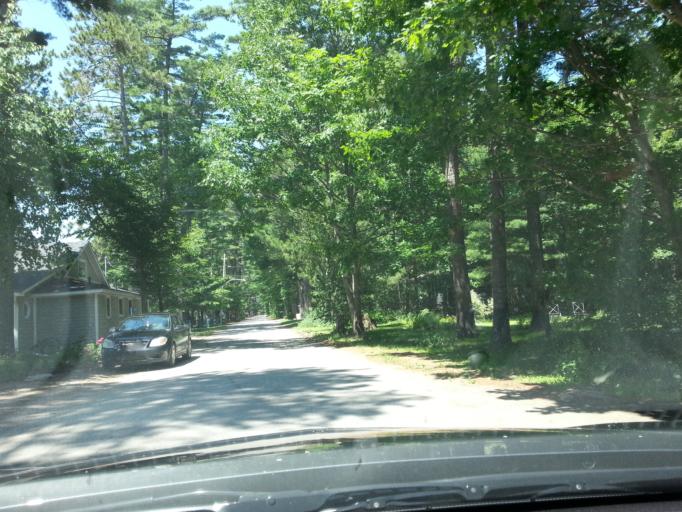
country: CA
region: Ontario
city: Arnprior
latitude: 45.5156
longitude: -76.4120
